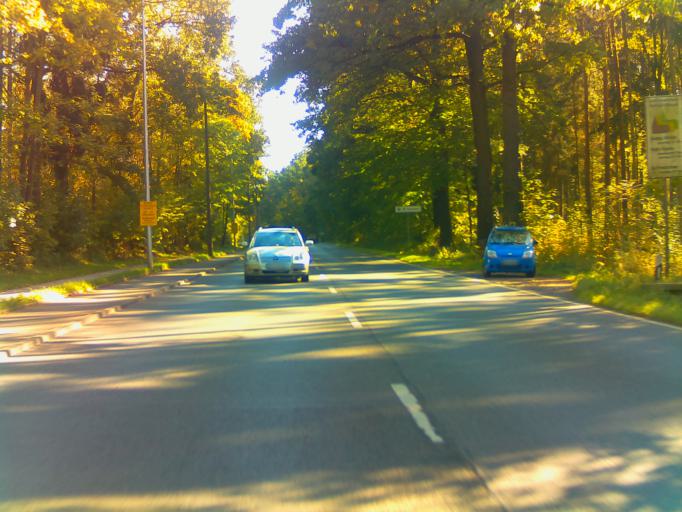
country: DE
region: Thuringia
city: Gera
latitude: 50.8666
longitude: 12.0488
